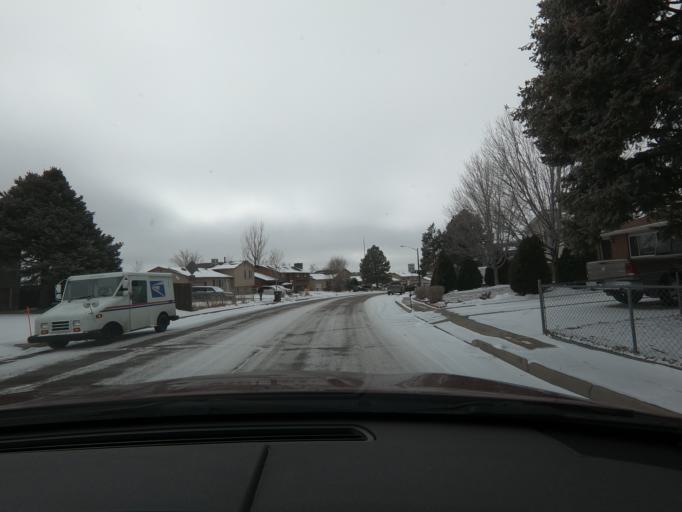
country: US
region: Colorado
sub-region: El Paso County
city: Security-Widefield
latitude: 38.7238
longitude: -104.6967
